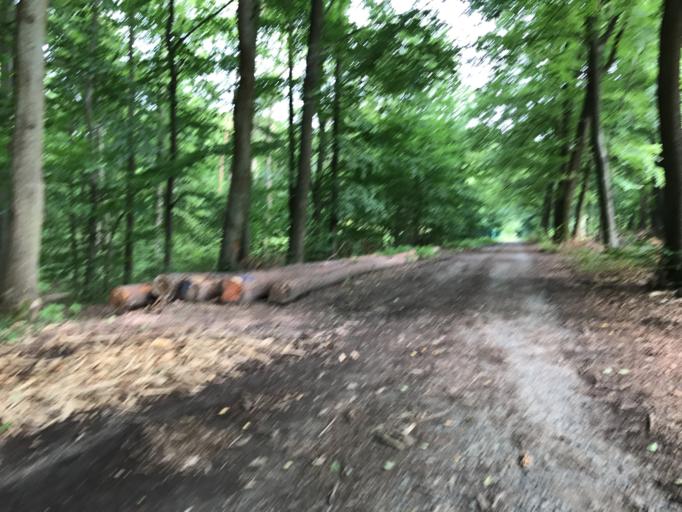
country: DE
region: Hesse
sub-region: Regierungsbezirk Darmstadt
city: Walluf
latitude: 50.0794
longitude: 8.1689
